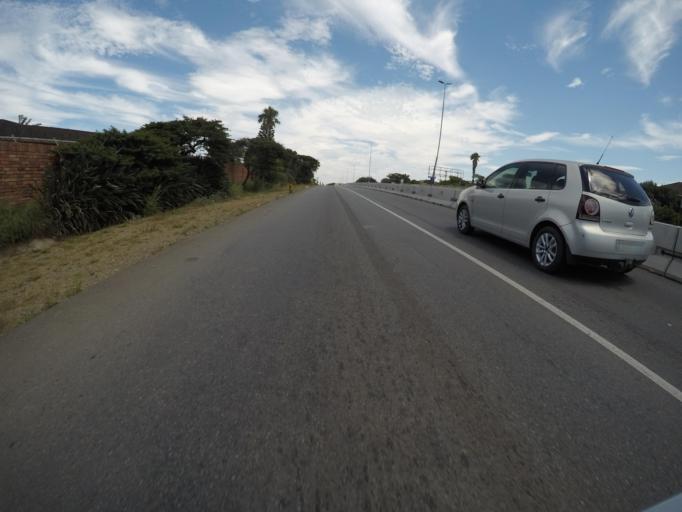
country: ZA
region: Eastern Cape
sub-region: Buffalo City Metropolitan Municipality
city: East London
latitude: -33.0361
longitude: 27.8627
